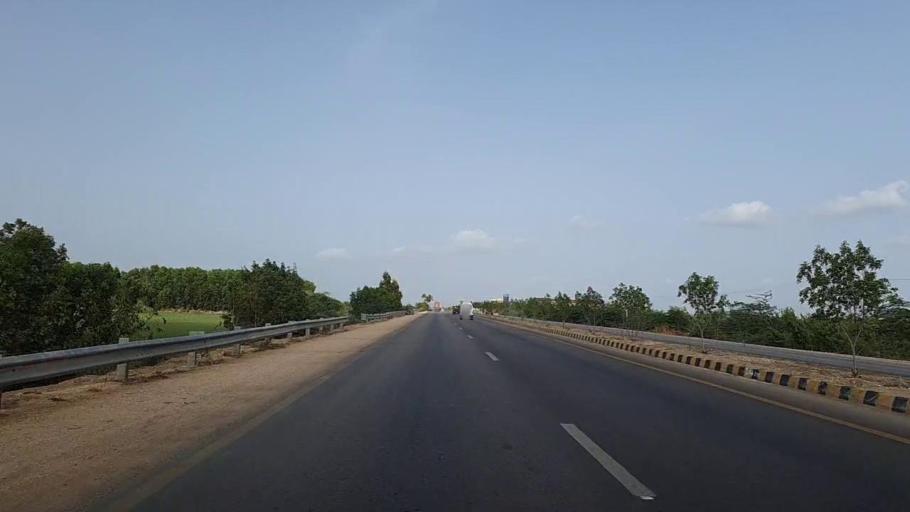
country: PK
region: Sindh
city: Gharo
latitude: 24.7324
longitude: 67.6795
